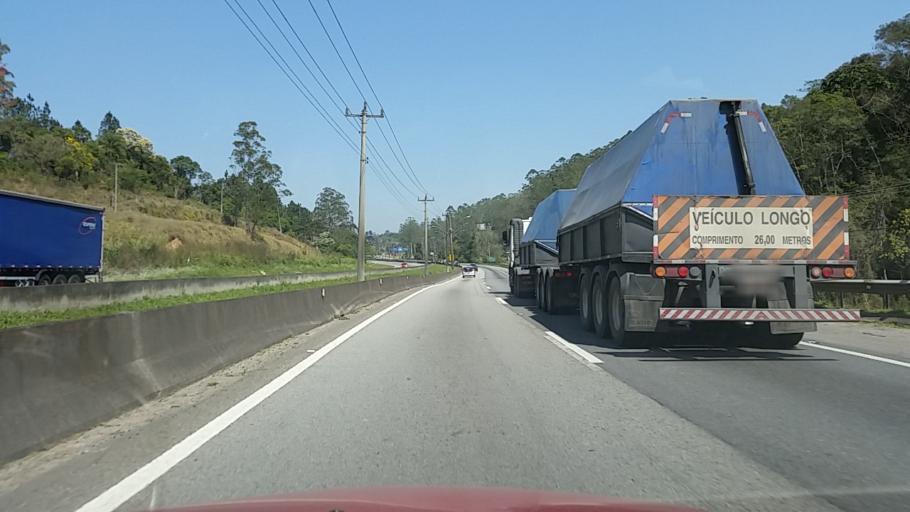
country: BR
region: Sao Paulo
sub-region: Itapecerica Da Serra
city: Itapecerica da Serra
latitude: -23.7709
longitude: -46.9114
